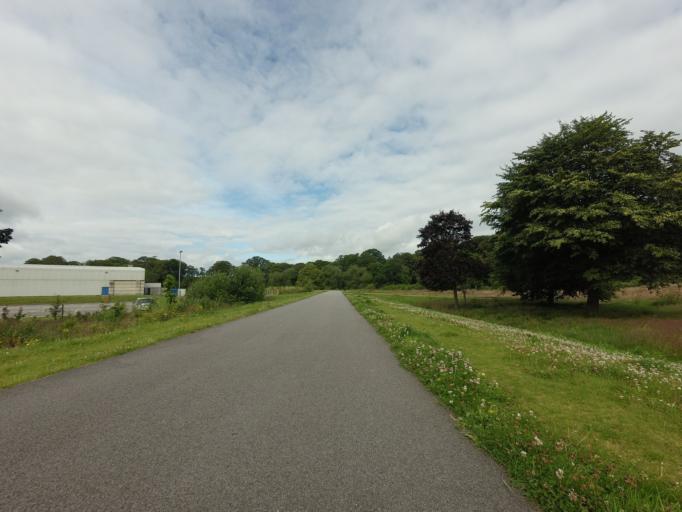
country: GB
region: Scotland
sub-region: Moray
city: Elgin
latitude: 57.6524
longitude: -3.3220
